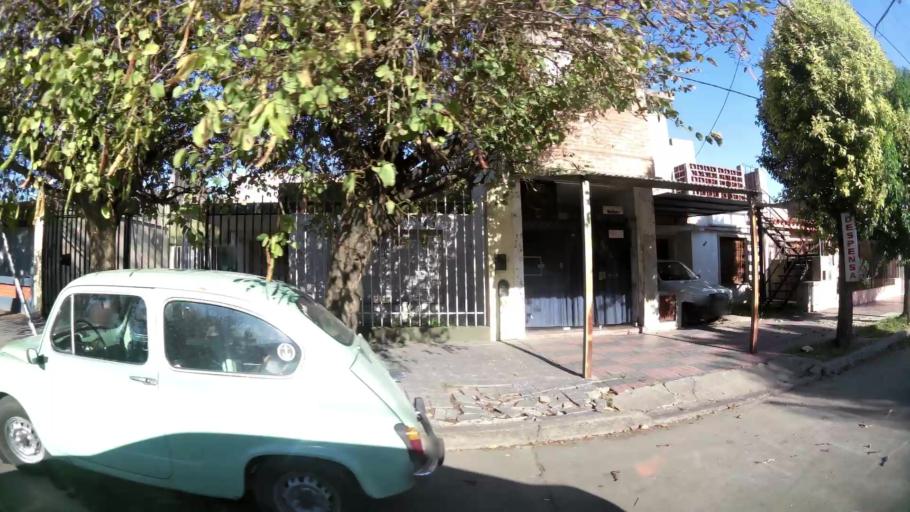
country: AR
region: Cordoba
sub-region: Departamento de Capital
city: Cordoba
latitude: -31.3796
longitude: -64.1772
